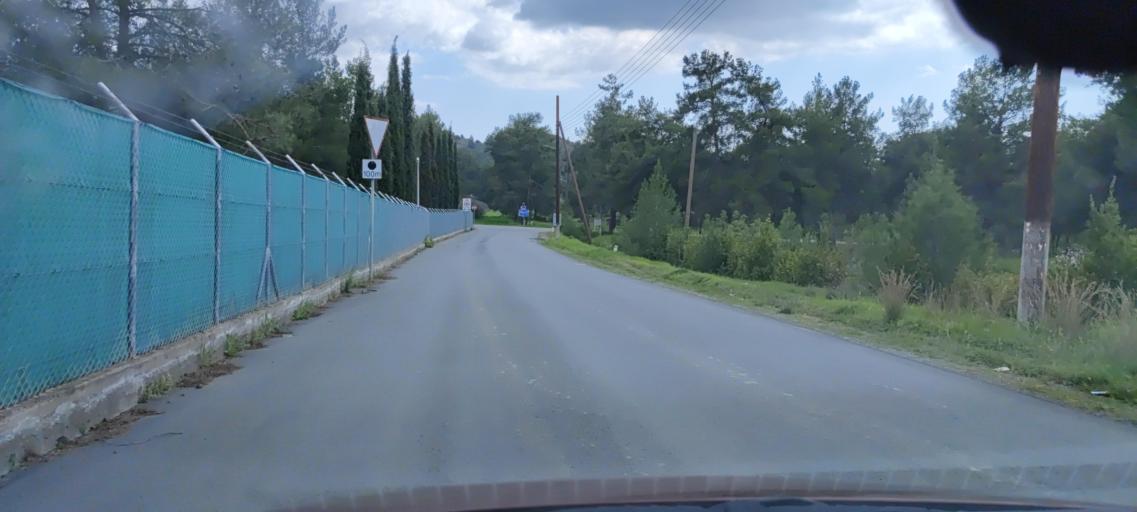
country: CY
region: Larnaka
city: Kornos
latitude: 34.9148
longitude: 33.3647
